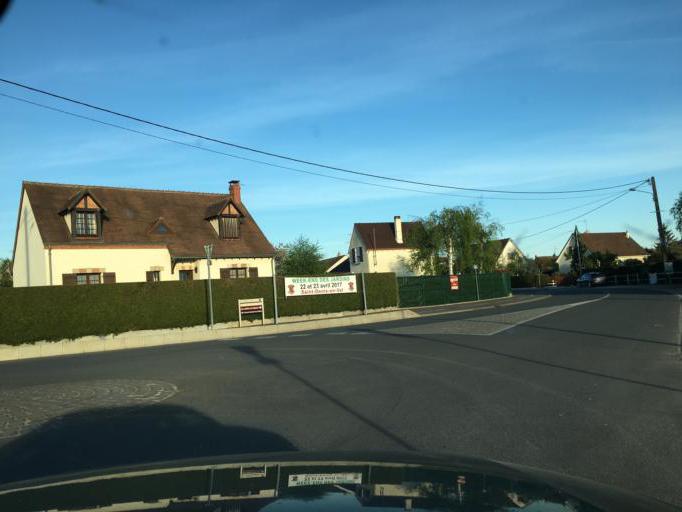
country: FR
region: Centre
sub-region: Departement du Loiret
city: Saint-Jean-le-Blanc
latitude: 47.8826
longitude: 1.9389
